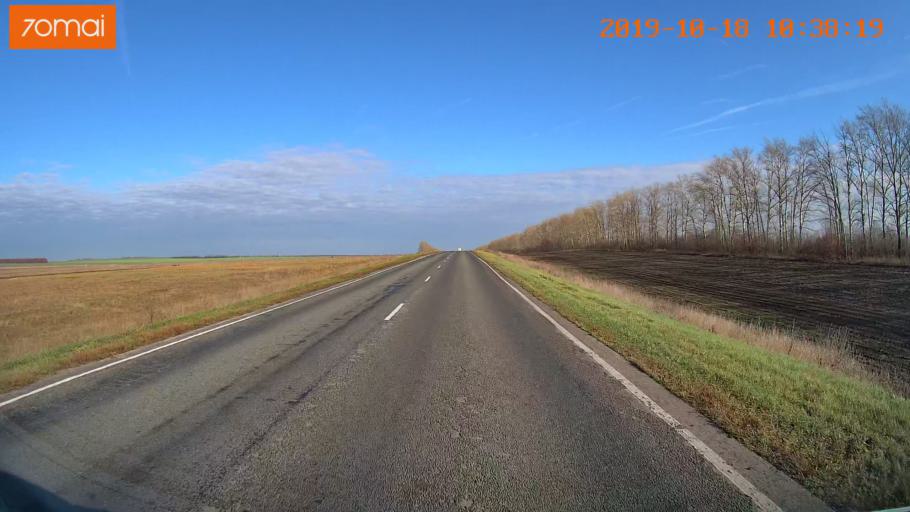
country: RU
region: Tula
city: Kurkino
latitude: 53.5713
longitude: 38.6401
